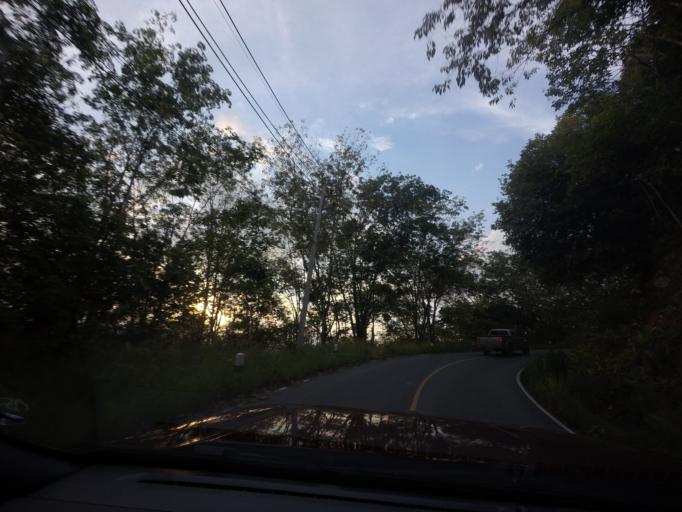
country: TH
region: Yala
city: Than To
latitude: 6.0070
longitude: 101.2202
